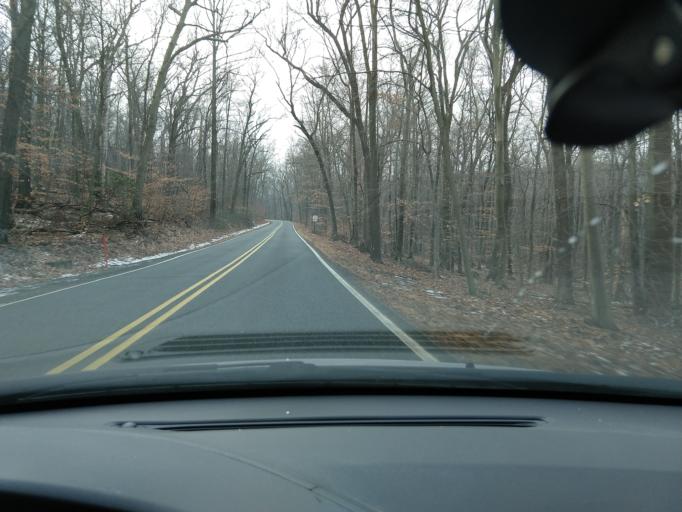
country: US
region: Pennsylvania
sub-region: Berks County
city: Birdsboro
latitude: 40.2296
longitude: -75.7740
